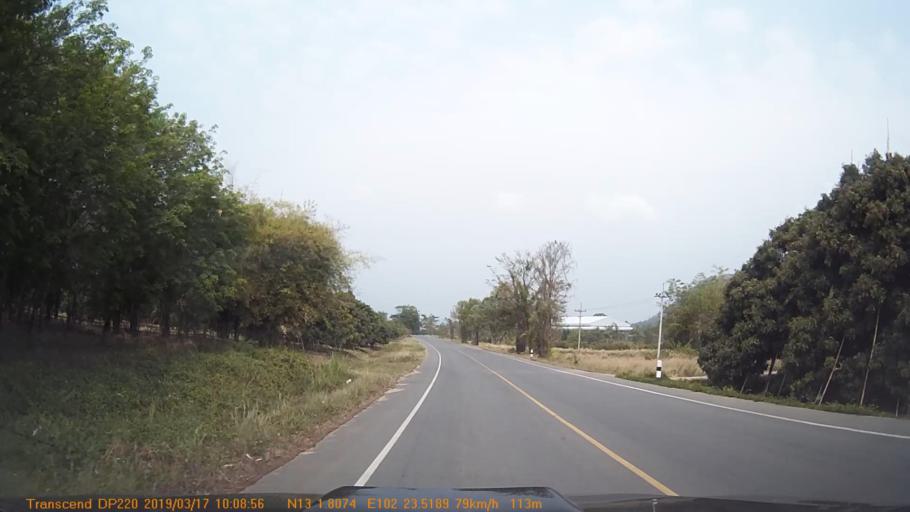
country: TH
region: Chanthaburi
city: Pong Nam Ron
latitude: 13.0310
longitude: 102.3897
